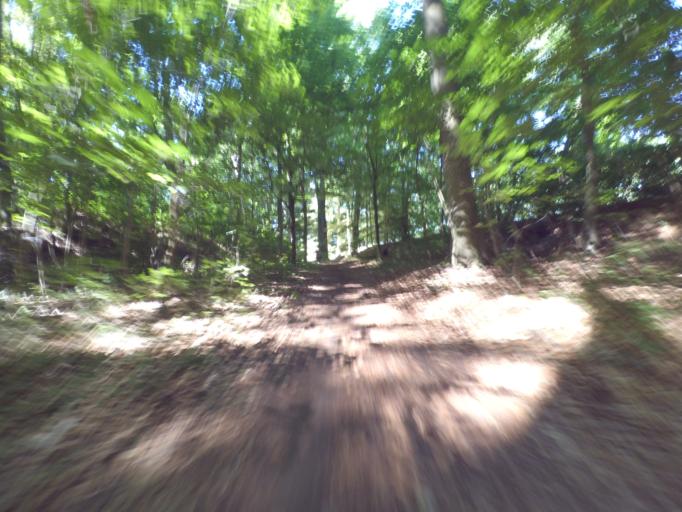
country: DE
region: Mecklenburg-Vorpommern
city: Malchow
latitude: 53.4787
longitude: 12.3639
